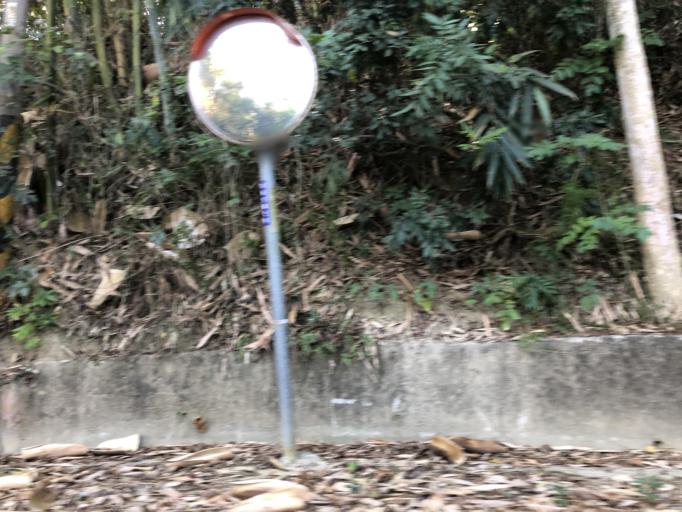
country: TW
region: Taiwan
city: Yujing
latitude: 23.0226
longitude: 120.3831
